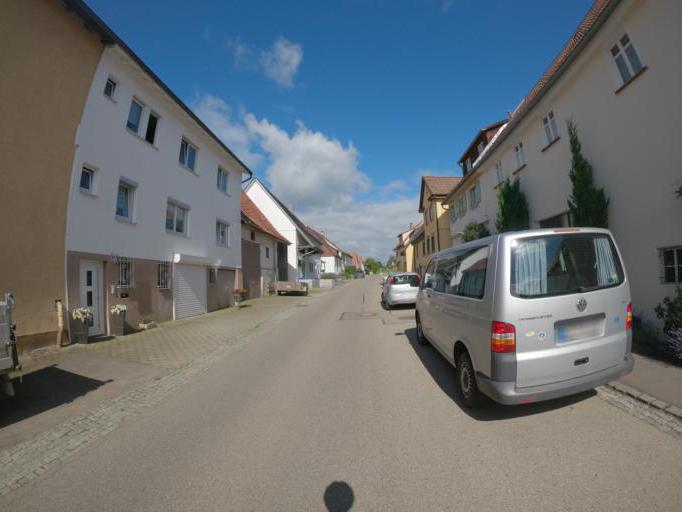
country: DE
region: Baden-Wuerttemberg
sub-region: Regierungsbezirk Stuttgart
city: Ebersbach an der Fils
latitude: 48.7260
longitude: 9.5487
